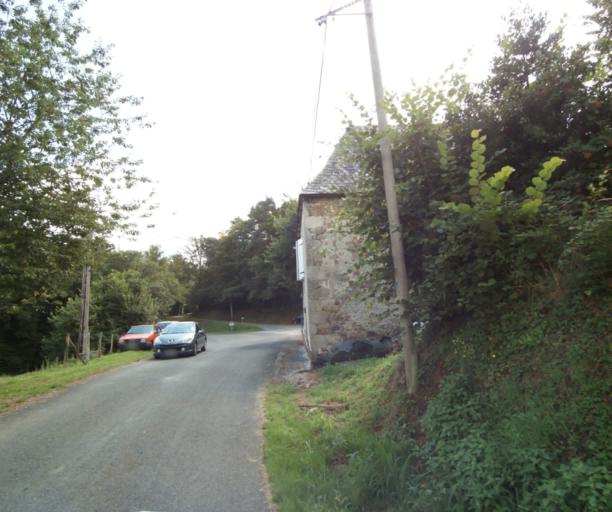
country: FR
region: Limousin
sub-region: Departement de la Correze
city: Sainte-Fortunade
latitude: 45.2034
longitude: 1.8449
